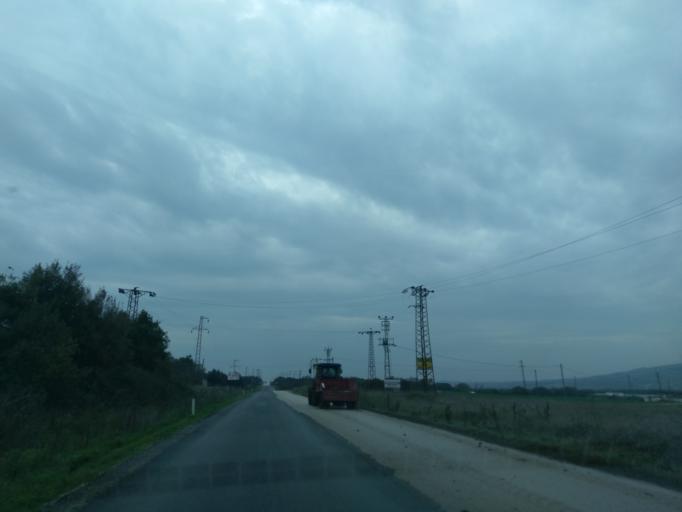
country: TR
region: Istanbul
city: Canta
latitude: 41.1450
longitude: 28.1069
